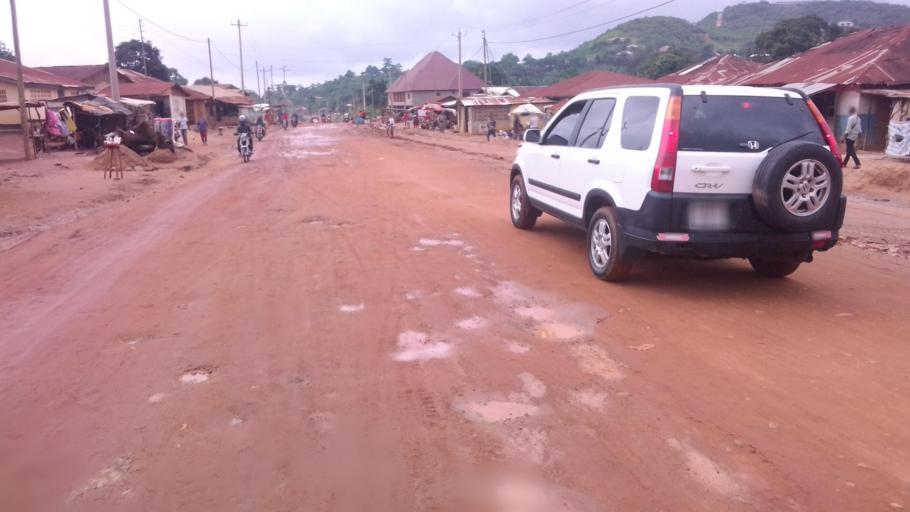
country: SL
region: Eastern Province
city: Kenema
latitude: 7.8571
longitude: -11.1853
